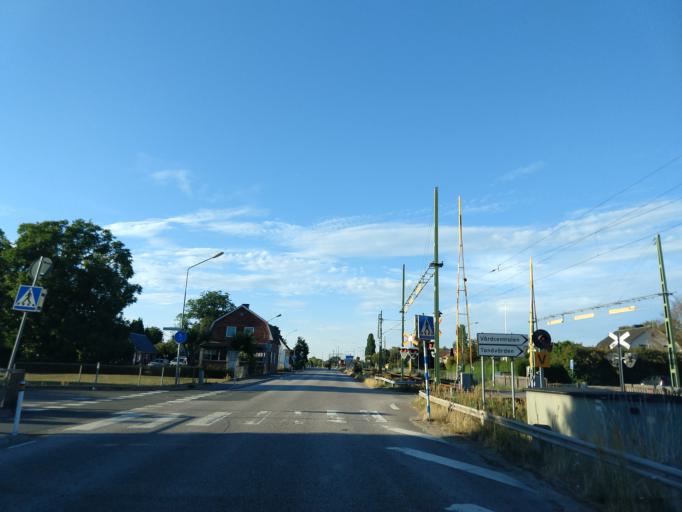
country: SE
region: Blekinge
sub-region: Ronneby Kommun
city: Brakne-Hoby
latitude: 56.2278
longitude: 15.1144
